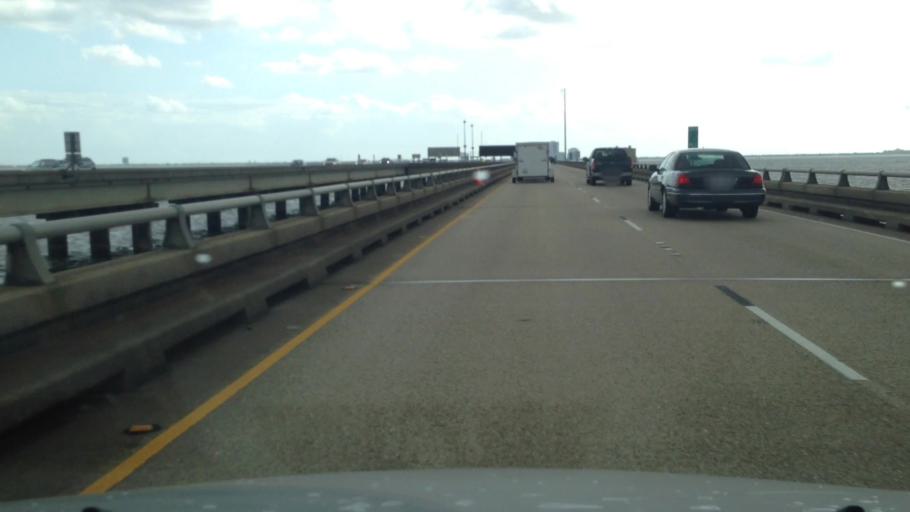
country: US
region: Louisiana
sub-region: Jefferson Parish
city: Metairie
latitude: 30.0723
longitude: -90.1452
